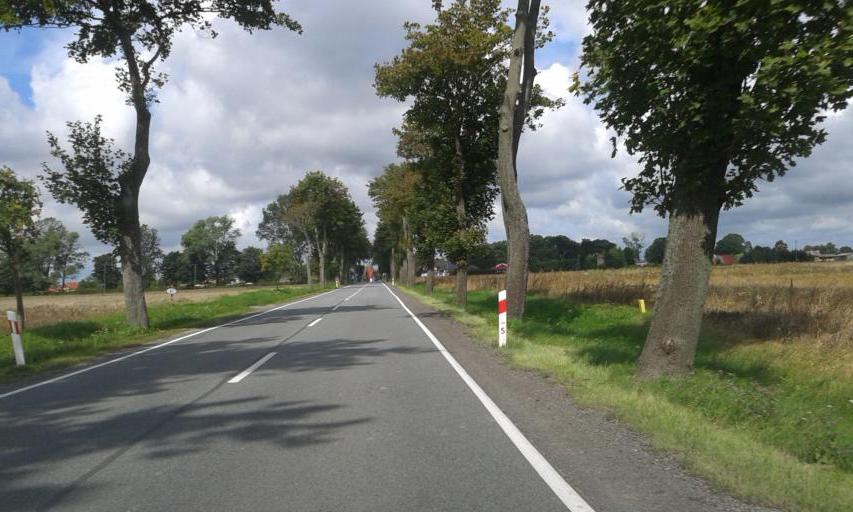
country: PL
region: West Pomeranian Voivodeship
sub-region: Powiat slawienski
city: Darlowo
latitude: 54.3547
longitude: 16.5221
